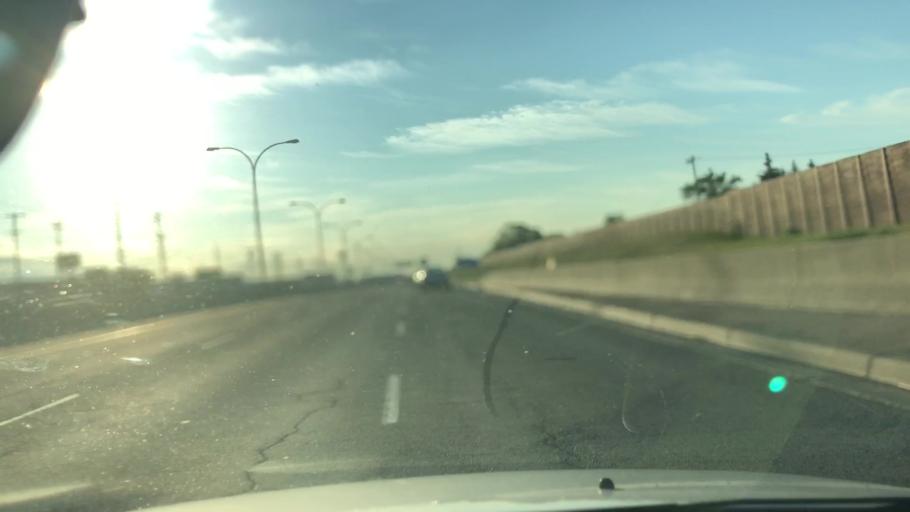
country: CA
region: Alberta
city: Edmonton
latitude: 53.5822
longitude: -113.4642
